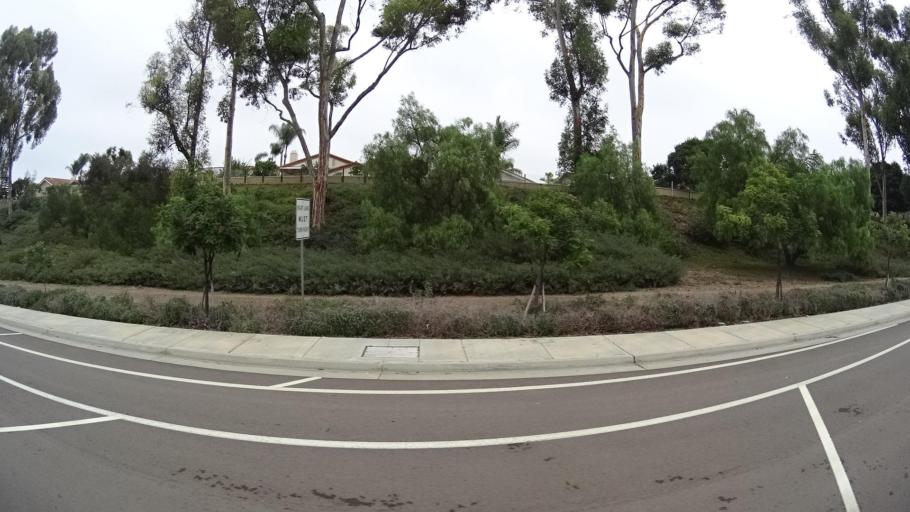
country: US
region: California
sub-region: San Diego County
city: Poway
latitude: 32.9956
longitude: -117.0794
